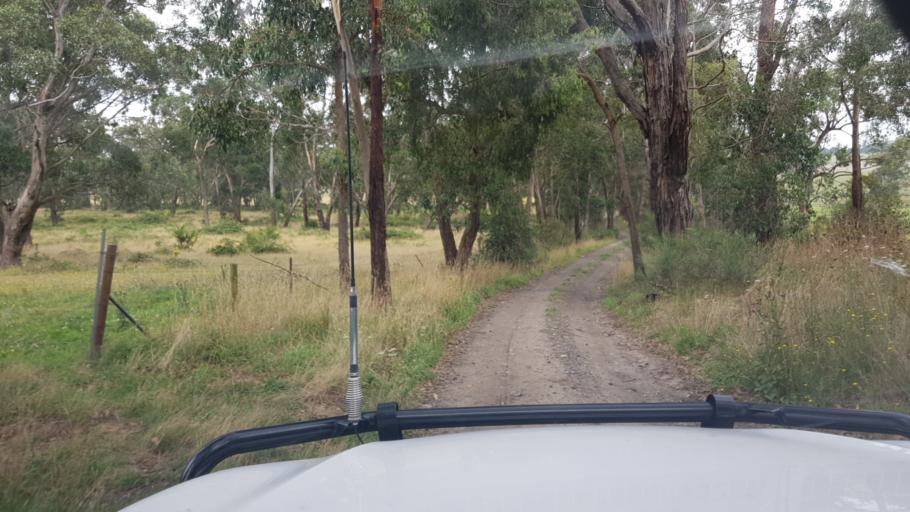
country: AU
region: Victoria
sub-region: Baw Baw
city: Warragul
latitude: -38.1384
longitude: 146.0385
